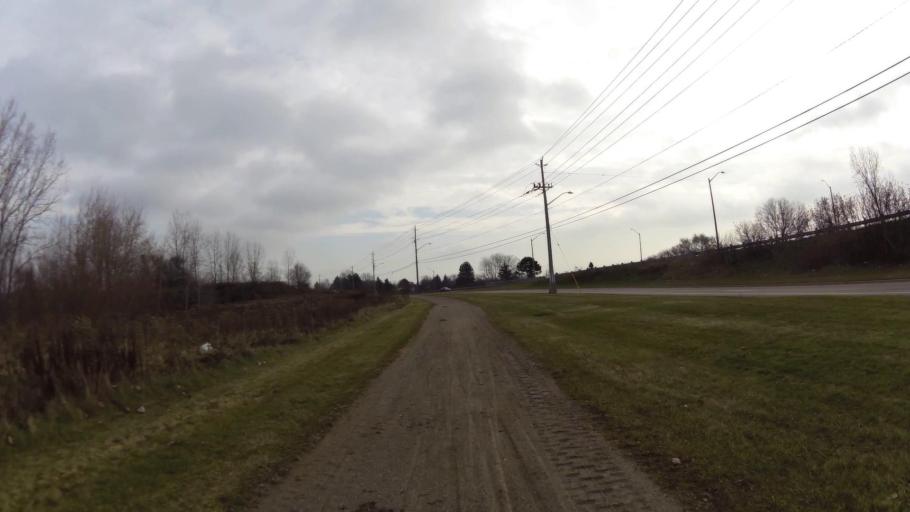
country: CA
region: Ontario
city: Kitchener
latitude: 43.3989
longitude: -80.4527
